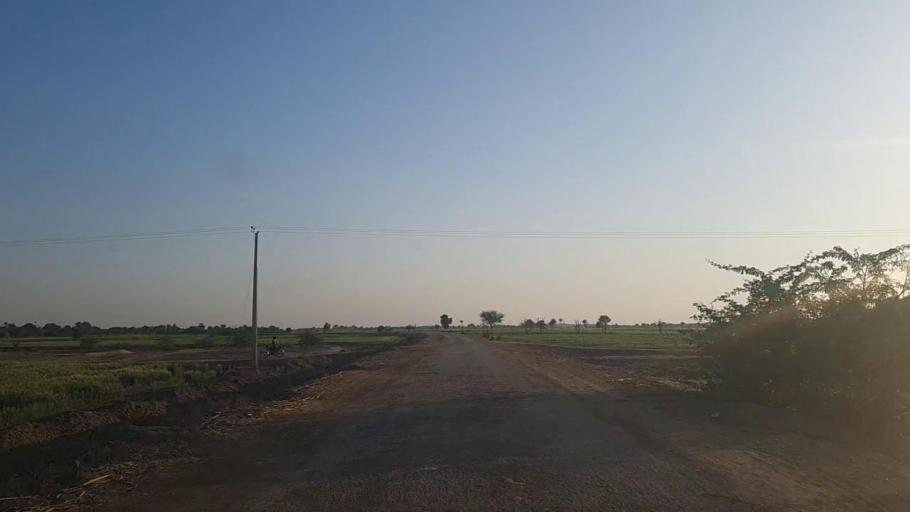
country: PK
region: Sindh
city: Jam Sahib
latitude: 26.3384
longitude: 68.6957
